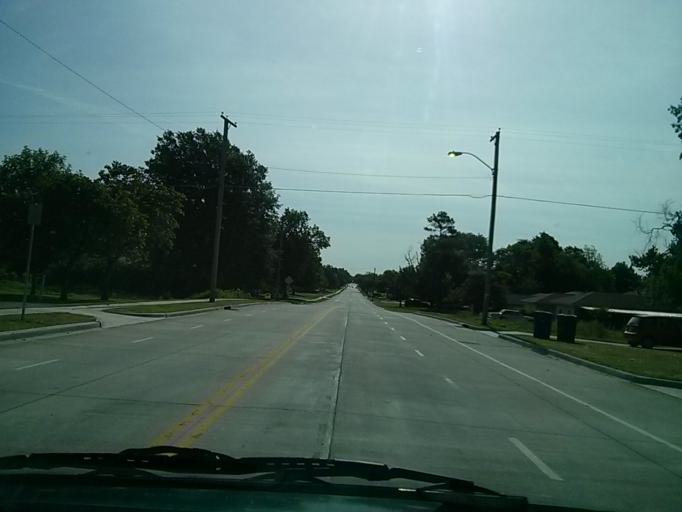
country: US
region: Oklahoma
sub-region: Tulsa County
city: Tulsa
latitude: 36.1551
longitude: -95.9157
